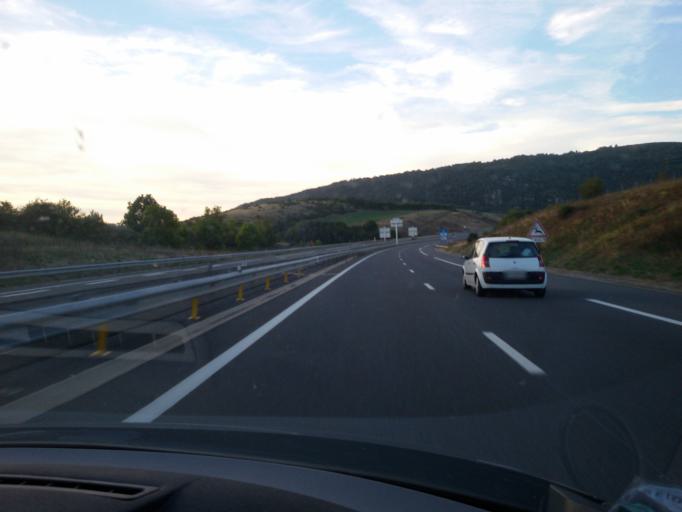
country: FR
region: Midi-Pyrenees
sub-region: Departement de l'Aveyron
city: Severac-le-Chateau
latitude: 44.3347
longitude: 3.0838
